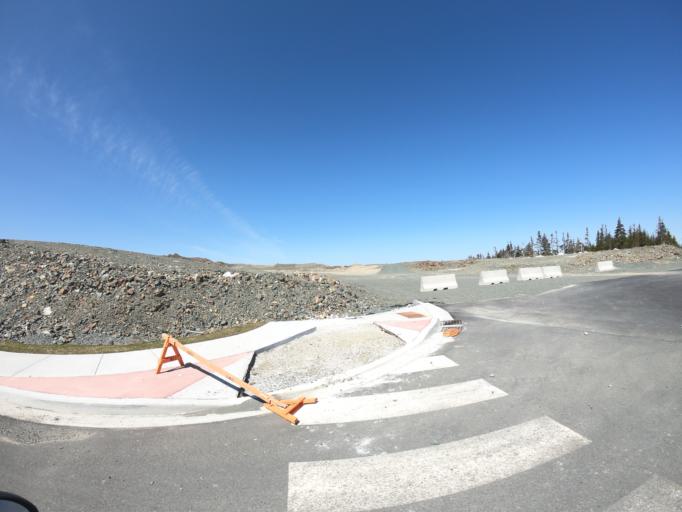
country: CA
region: Newfoundland and Labrador
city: Mount Pearl
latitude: 47.5089
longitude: -52.8360
